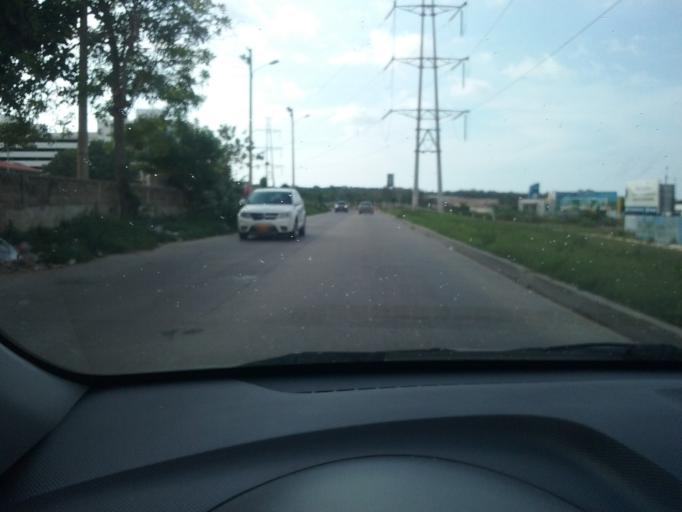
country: CO
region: Atlantico
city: Barranquilla
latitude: 11.0195
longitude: -74.8191
